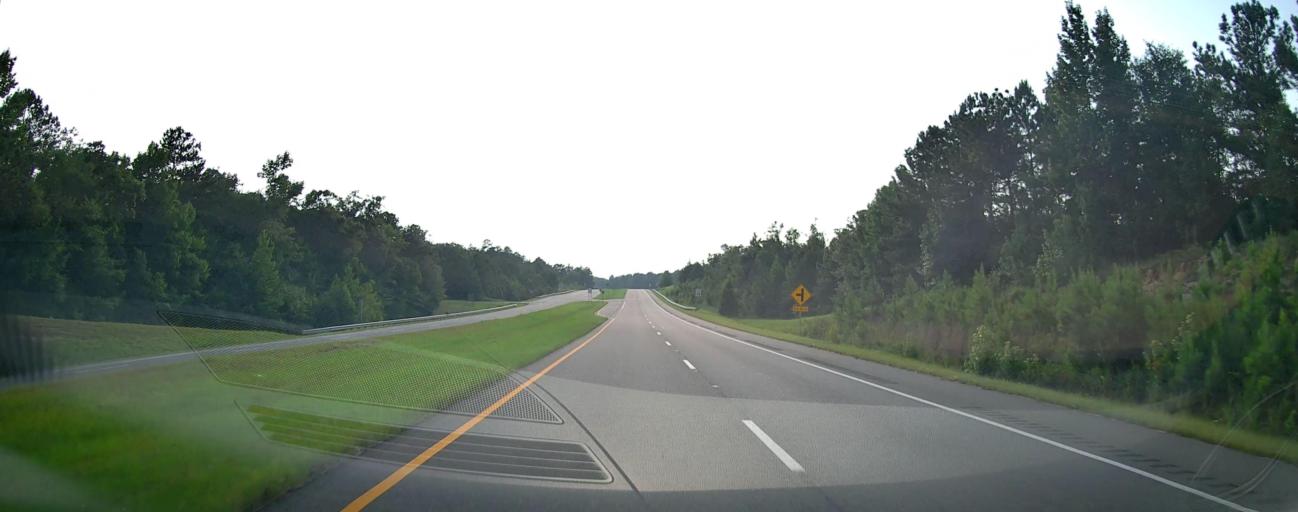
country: US
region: Georgia
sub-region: Talbot County
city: Talbotton
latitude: 32.5798
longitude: -84.5393
